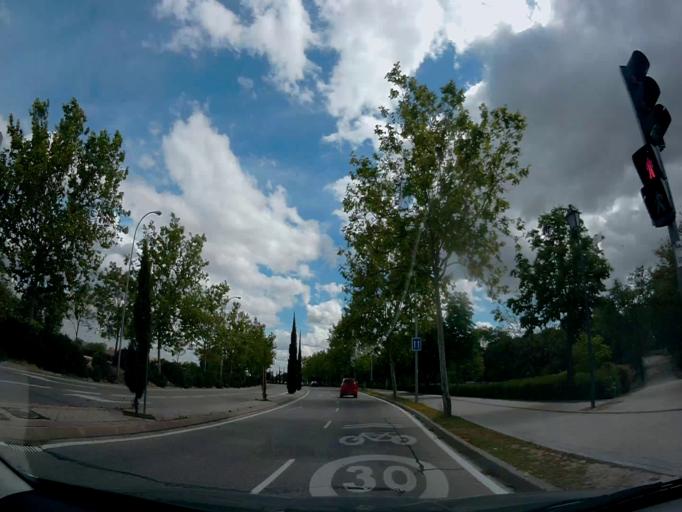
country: ES
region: Madrid
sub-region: Provincia de Madrid
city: Vicalvaro
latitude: 40.4049
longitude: -3.6173
